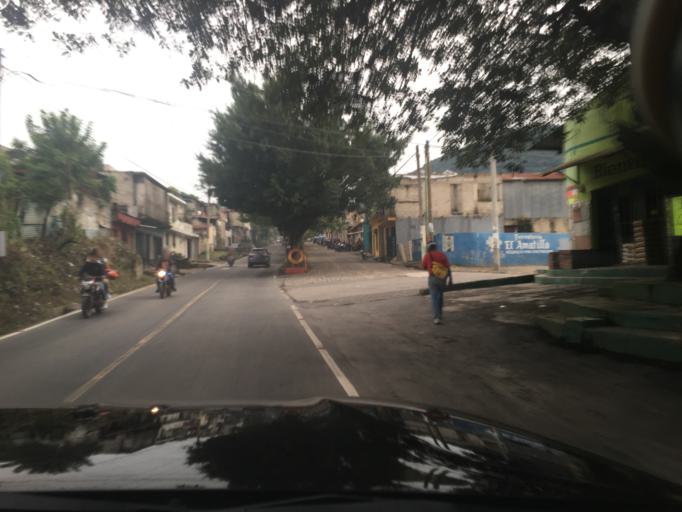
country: GT
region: Guatemala
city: Amatitlan
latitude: 14.4807
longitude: -90.6146
